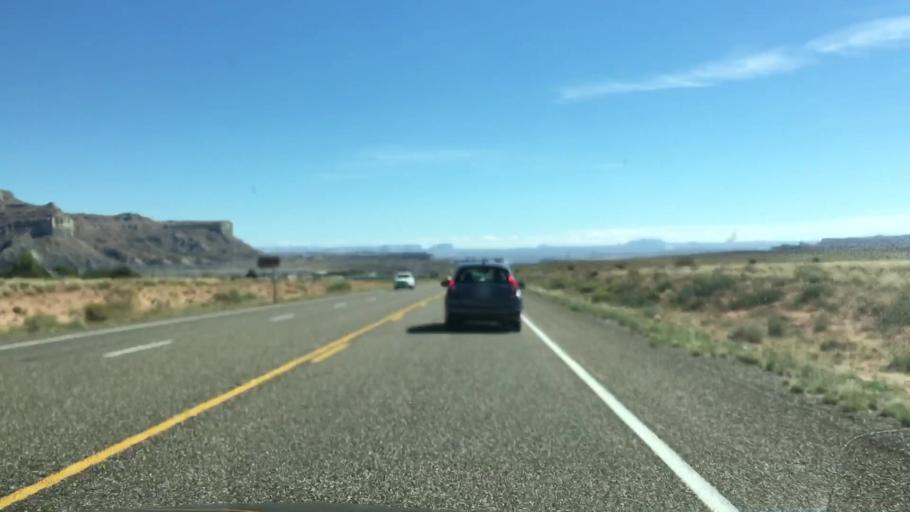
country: US
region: Arizona
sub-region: Coconino County
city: Page
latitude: 37.0809
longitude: -111.6706
